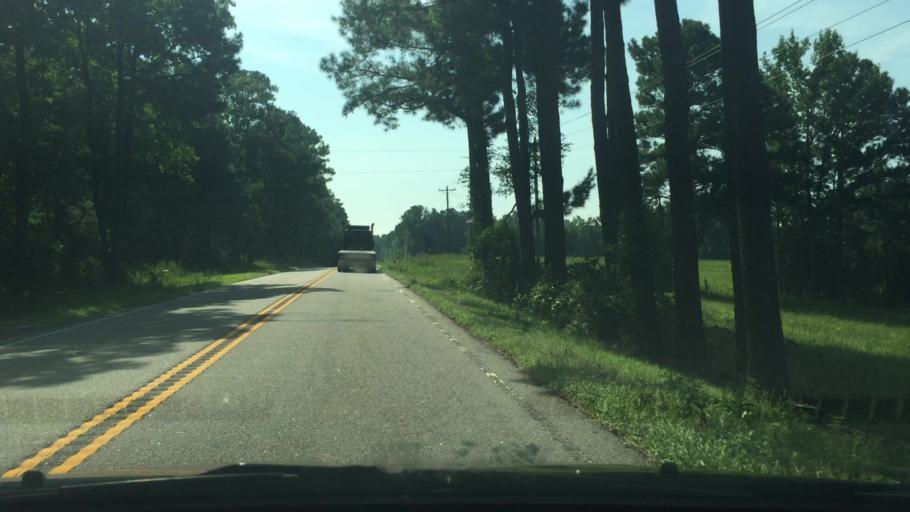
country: US
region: Virginia
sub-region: Sussex County
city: Sussex
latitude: 37.0355
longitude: -77.3063
